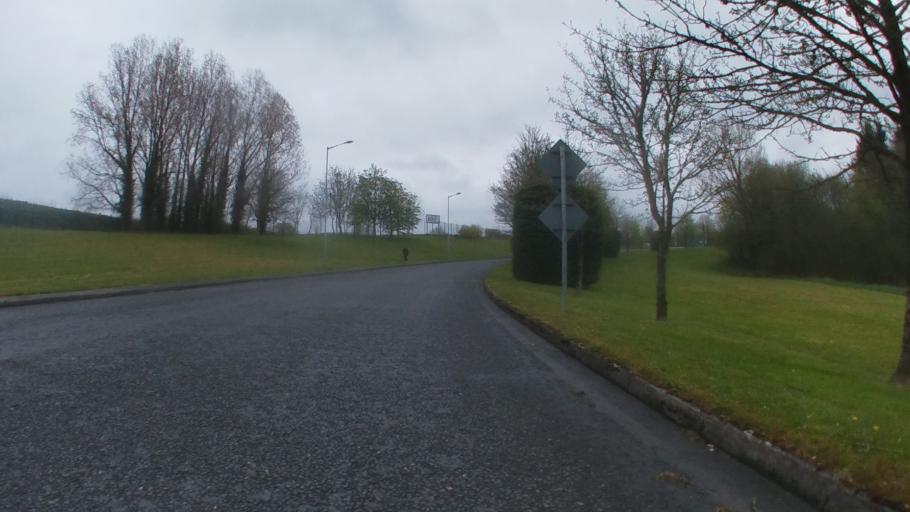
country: IE
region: Leinster
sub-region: Kilkenny
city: Kilkenny
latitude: 52.6475
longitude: -7.2177
